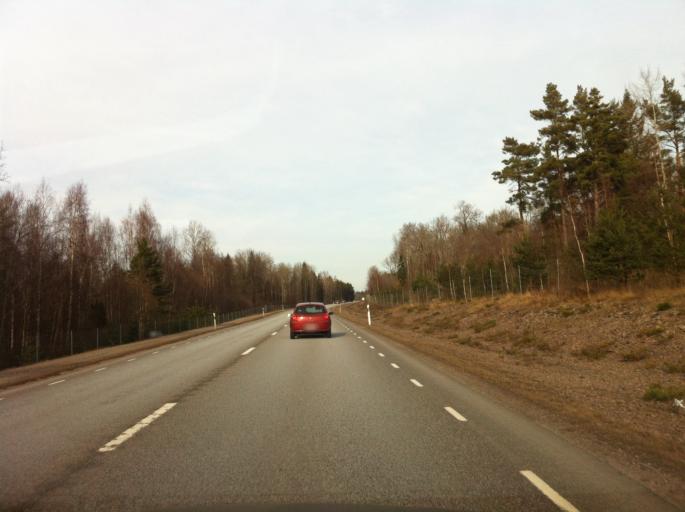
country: SE
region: Vaestra Goetaland
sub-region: Gullspangs Kommun
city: Gullspang
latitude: 58.9064
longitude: 14.0216
